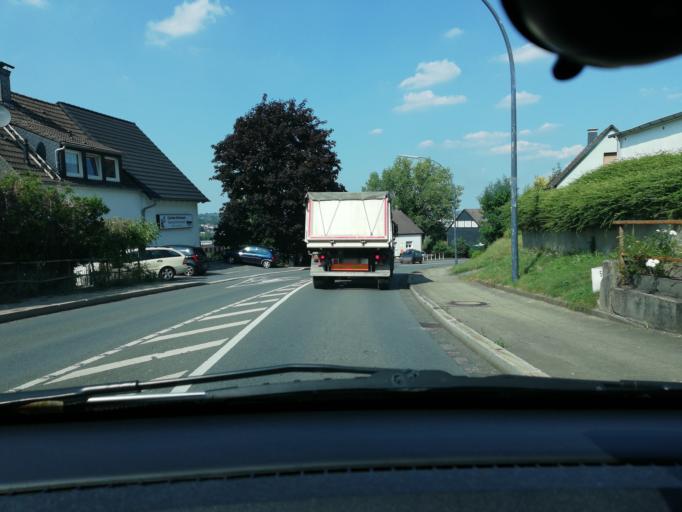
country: DE
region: North Rhine-Westphalia
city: Gevelsberg
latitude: 51.3126
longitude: 7.3241
